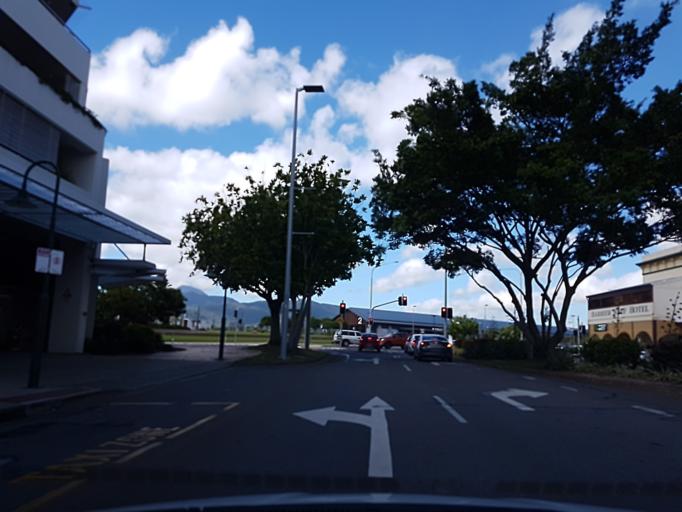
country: AU
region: Queensland
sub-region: Cairns
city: Cairns
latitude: -16.9243
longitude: 145.7795
